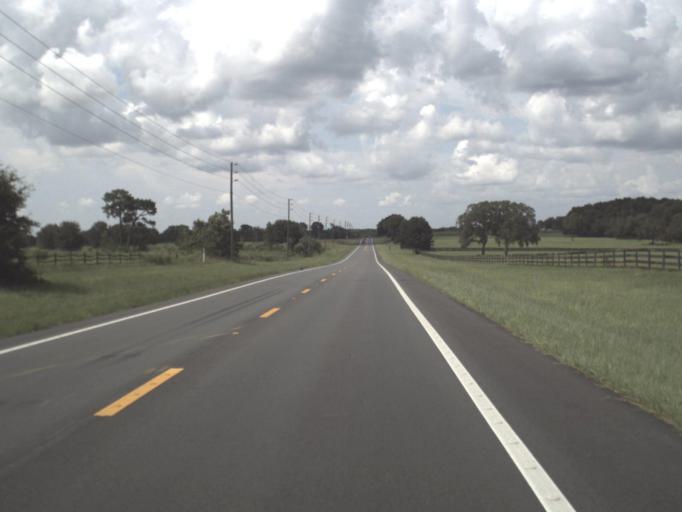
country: US
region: Florida
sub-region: Citrus County
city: Floral City
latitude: 28.7037
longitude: -82.3140
